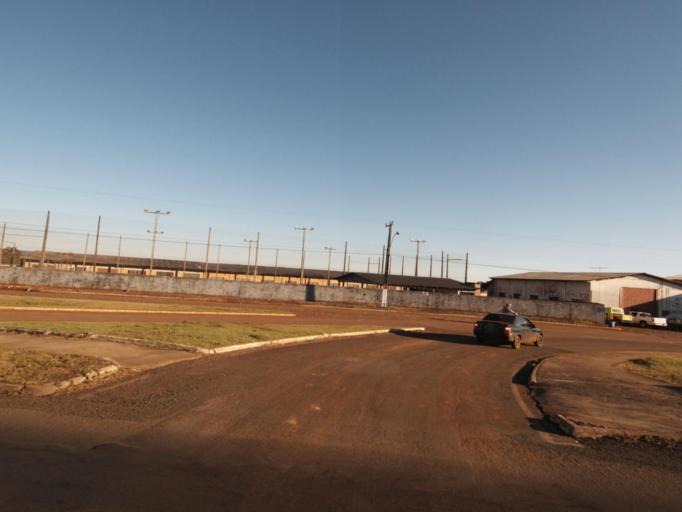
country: BR
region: Santa Catarina
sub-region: Chapeco
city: Chapeco
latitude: -26.9053
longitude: -52.9038
